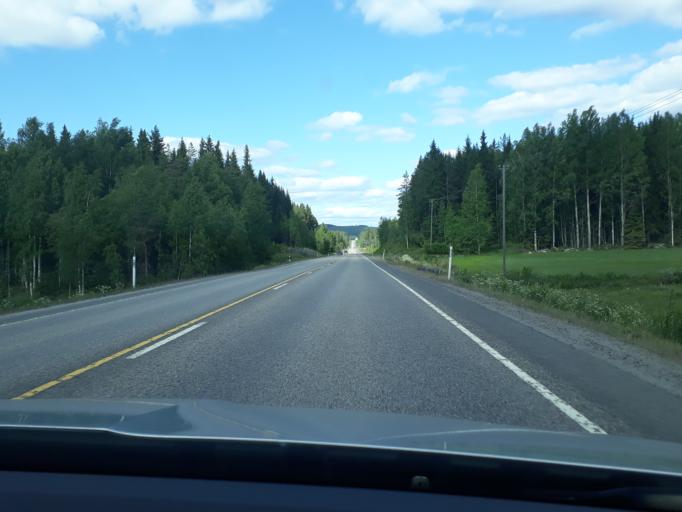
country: FI
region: Central Finland
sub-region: AEaenekoski
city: AEaenekoski
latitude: 62.6494
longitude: 25.7148
